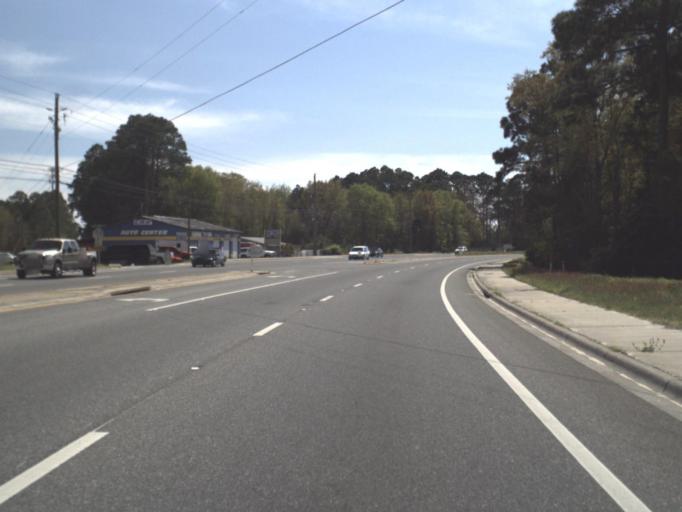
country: US
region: Florida
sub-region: Bay County
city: Lynn Haven
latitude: 30.2709
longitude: -85.6409
